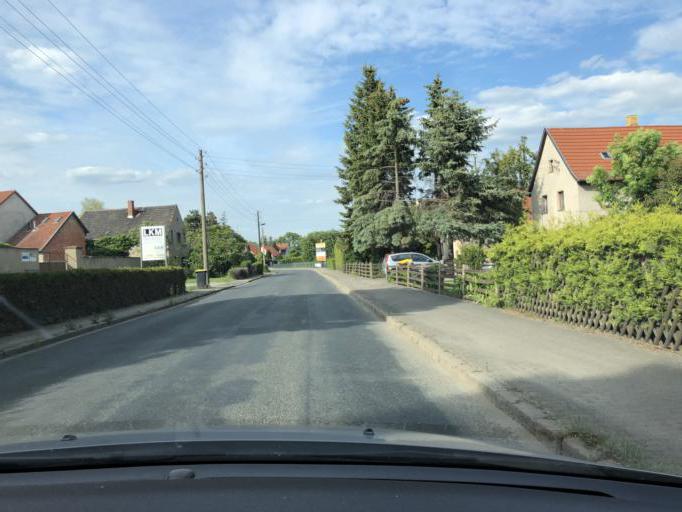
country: DE
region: Saxony
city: Borsdorf
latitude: 51.3245
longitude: 12.5274
